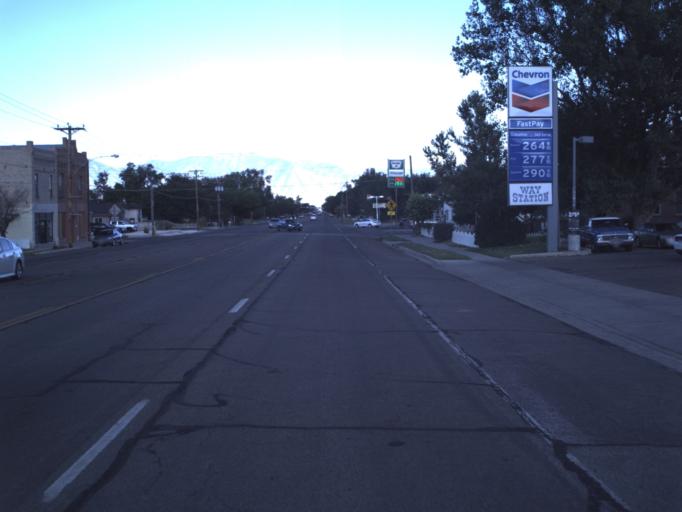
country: US
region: Utah
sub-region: Tooele County
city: Grantsville
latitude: 40.5998
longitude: -112.4651
